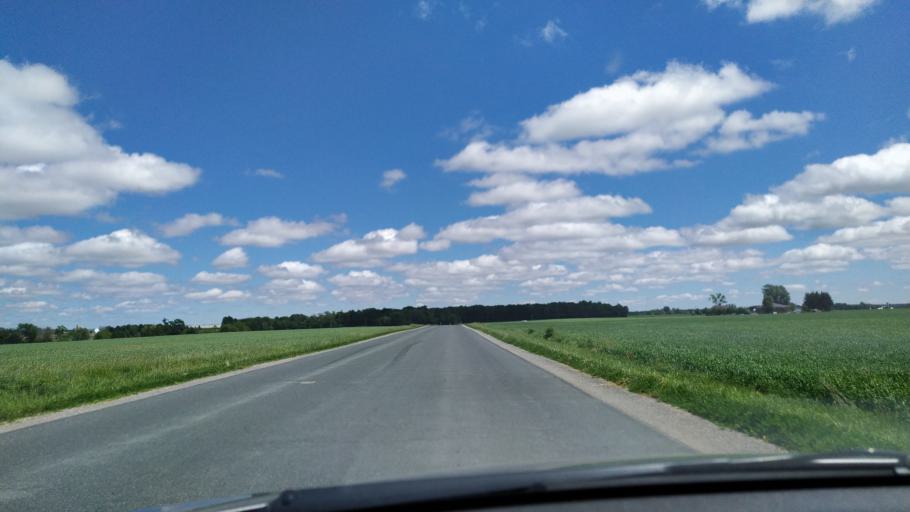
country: CA
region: Ontario
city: Huron East
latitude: 43.4536
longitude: -81.1894
